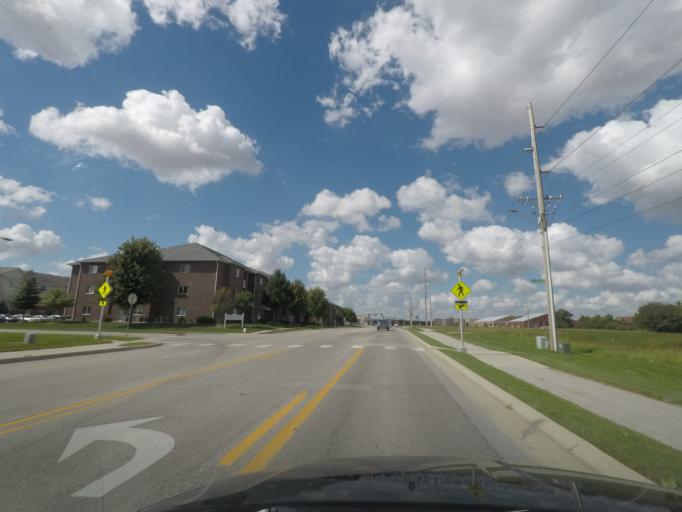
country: US
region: Iowa
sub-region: Story County
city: Ames
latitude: 42.0121
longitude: -93.6759
